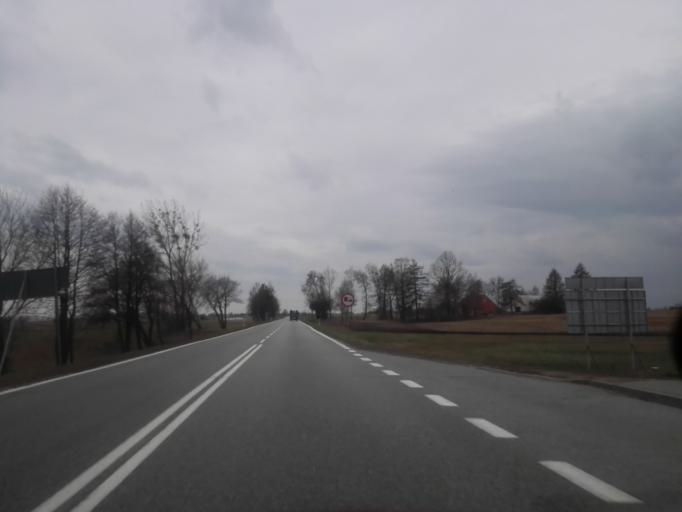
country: PL
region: Podlasie
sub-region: Powiat augustowski
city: Augustow
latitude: 53.8164
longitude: 22.9242
